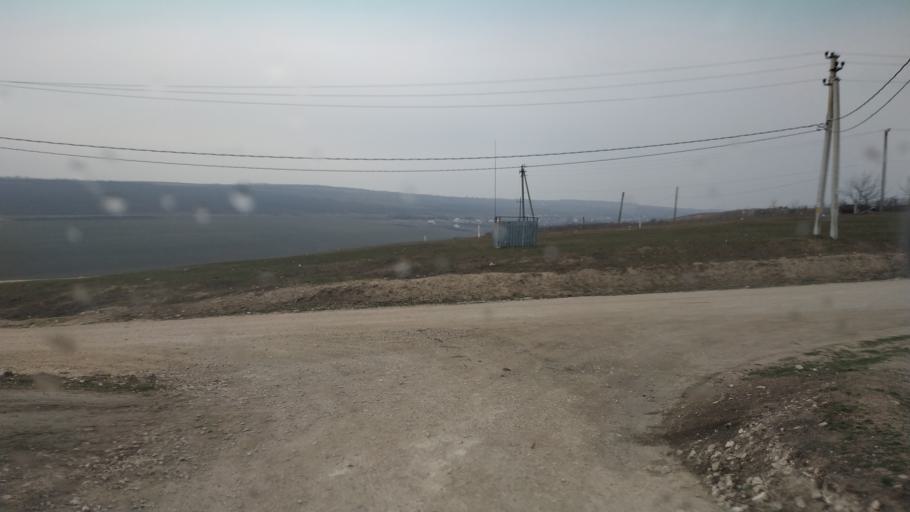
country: MD
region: Chisinau
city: Singera
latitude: 46.8261
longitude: 28.9624
